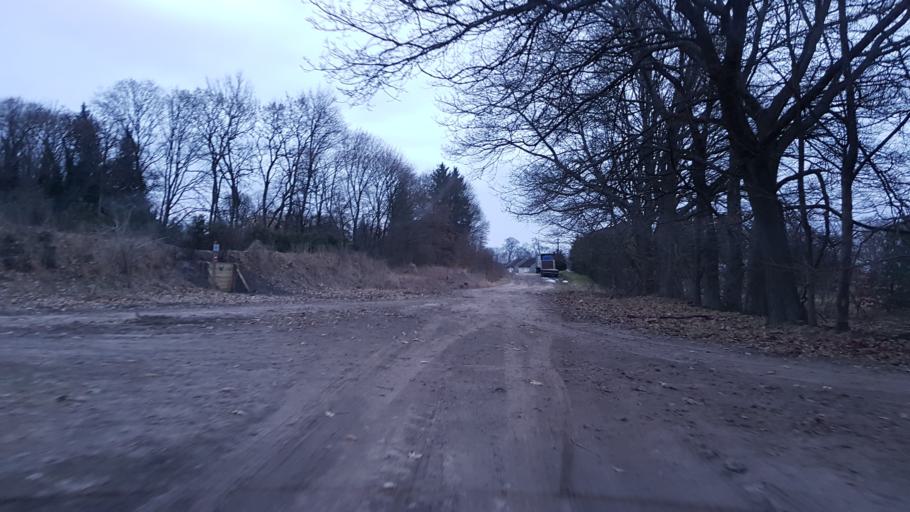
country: PL
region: Greater Poland Voivodeship
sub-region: Powiat zlotowski
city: Sypniewo
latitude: 53.4863
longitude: 16.6901
